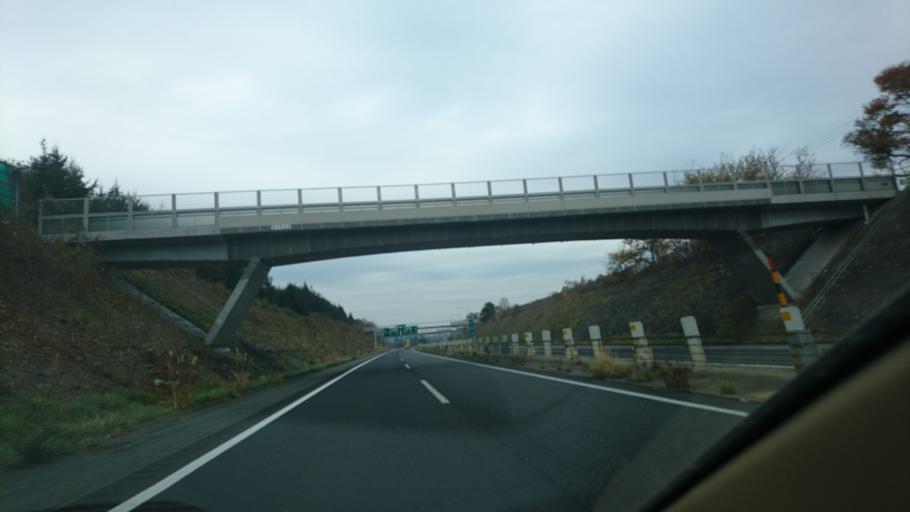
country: JP
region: Iwate
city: Kitakami
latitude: 39.2677
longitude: 141.0759
